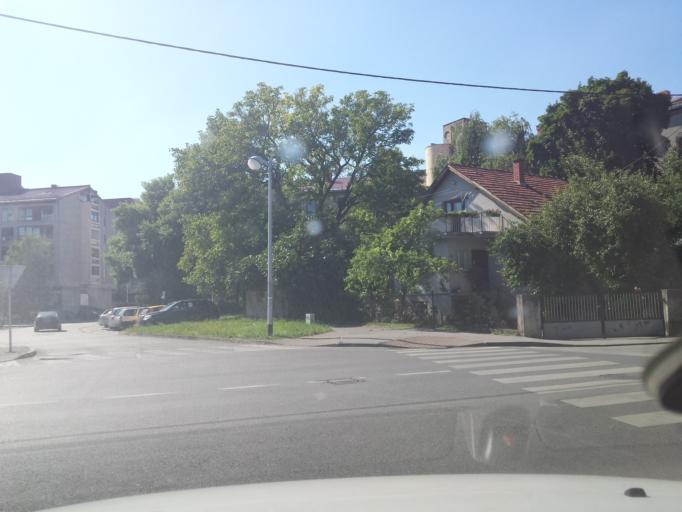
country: HR
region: Grad Zagreb
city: Jankomir
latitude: 45.8006
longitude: 15.8976
